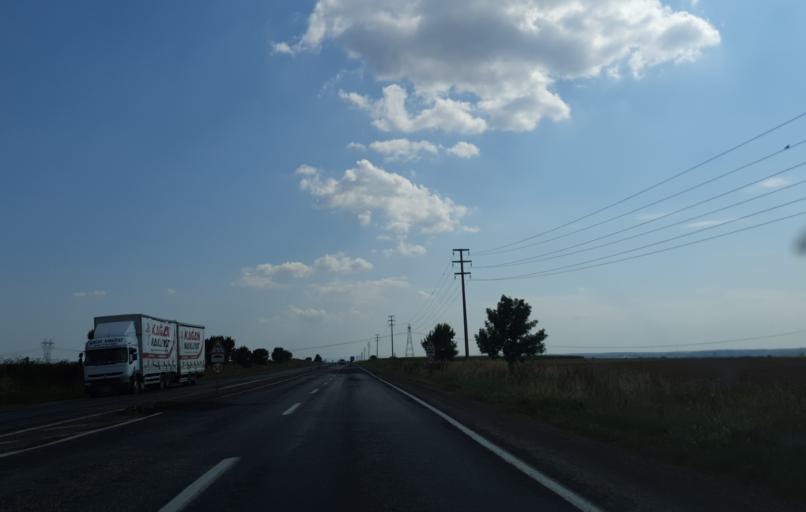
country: TR
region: Kirklareli
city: Buyukkaristiran
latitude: 41.2395
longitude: 27.5368
